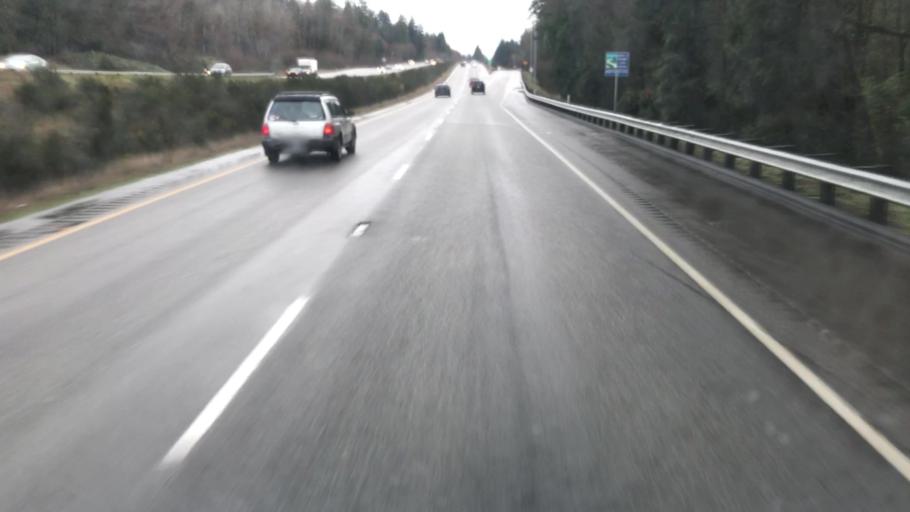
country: US
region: Washington
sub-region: Kitsap County
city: Burley
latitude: 47.4373
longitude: -122.6231
